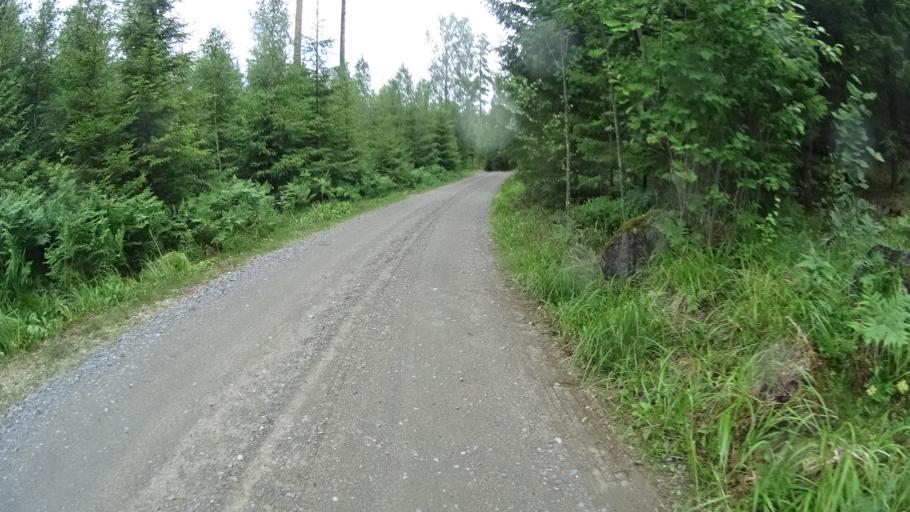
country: FI
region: Uusimaa
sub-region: Helsinki
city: Karkkila
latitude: 60.5799
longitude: 24.2797
